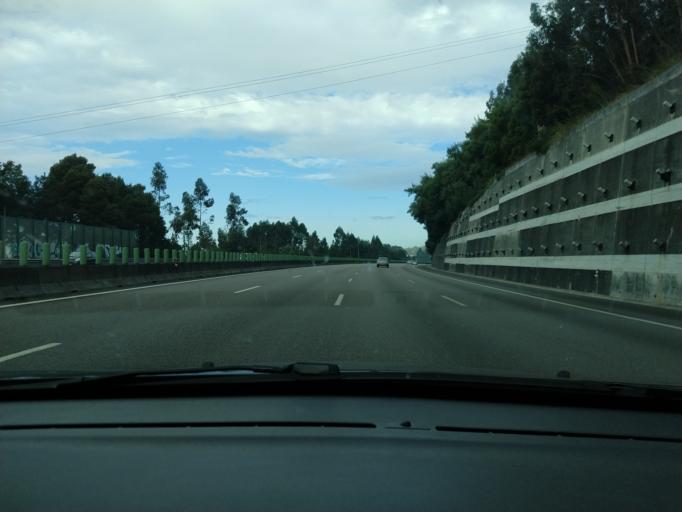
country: PT
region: Porto
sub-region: Vila Nova de Gaia
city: Perozinho
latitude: 41.0539
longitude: -8.5752
